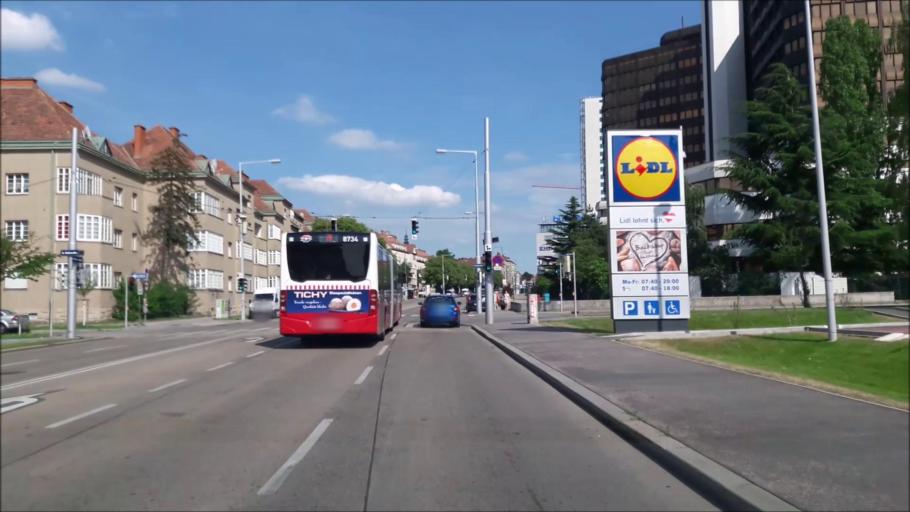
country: AT
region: Vienna
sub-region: Wien Stadt
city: Vienna
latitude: 48.1703
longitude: 16.3426
